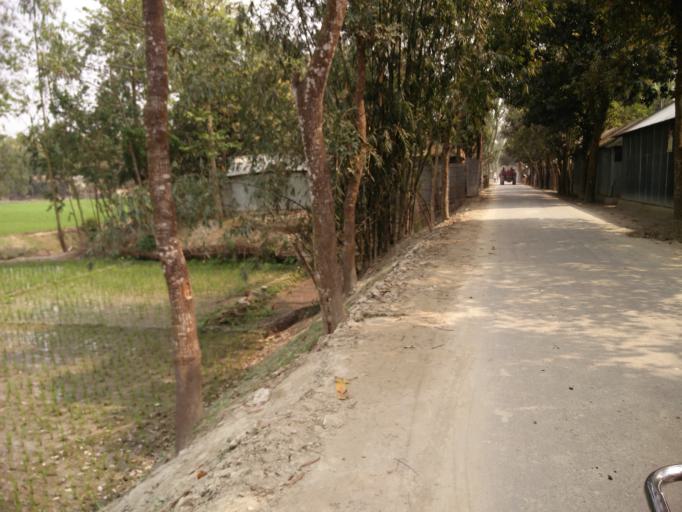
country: BD
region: Rangpur Division
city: Nageswari
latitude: 25.8861
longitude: 89.7397
